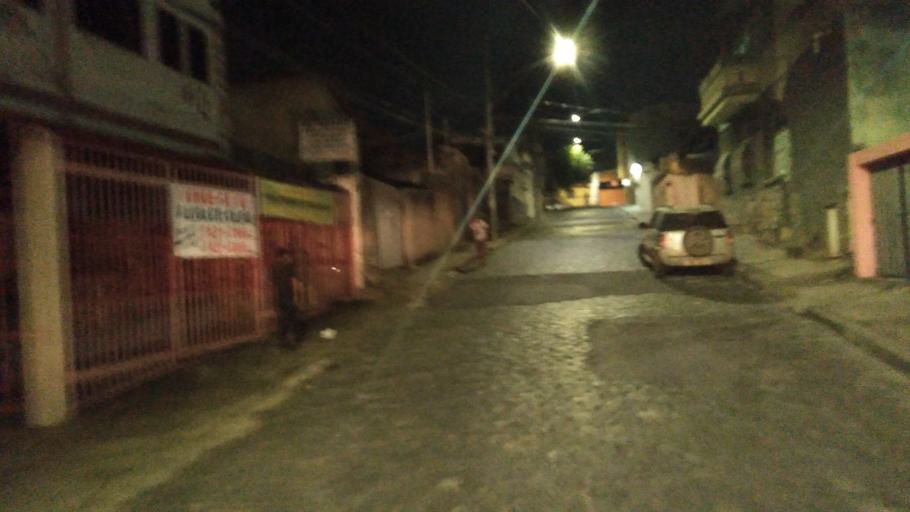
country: BR
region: Minas Gerais
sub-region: Belo Horizonte
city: Belo Horizonte
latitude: -19.9081
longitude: -43.9470
